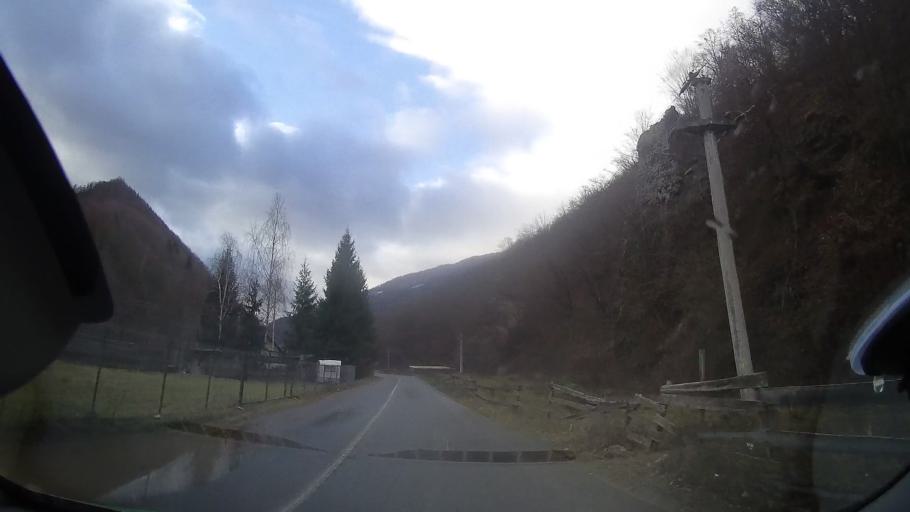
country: RO
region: Cluj
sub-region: Comuna Valea Ierii
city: Valea Ierii
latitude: 46.6863
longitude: 23.2765
